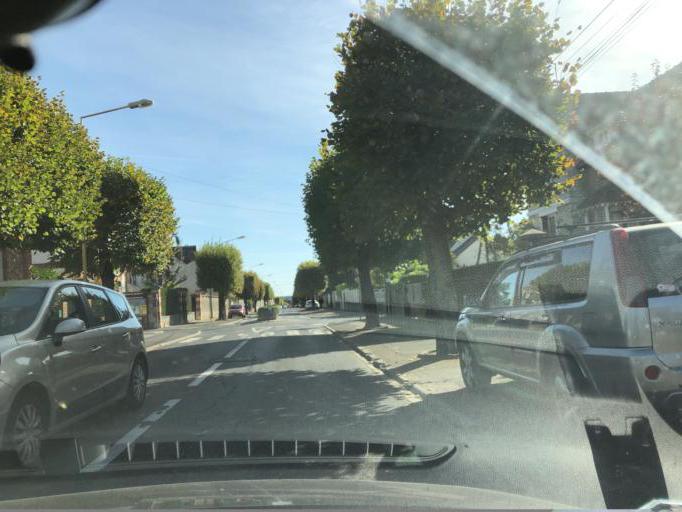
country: FR
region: Centre
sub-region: Departement du Loiret
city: Malesherbes
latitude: 48.2942
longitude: 2.4041
